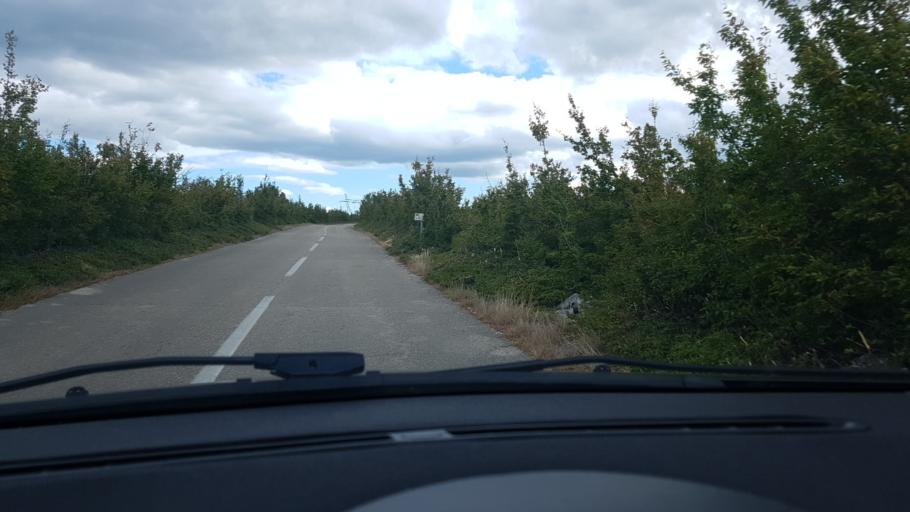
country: HR
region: Zadarska
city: Gracac
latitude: 44.1806
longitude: 15.8885
